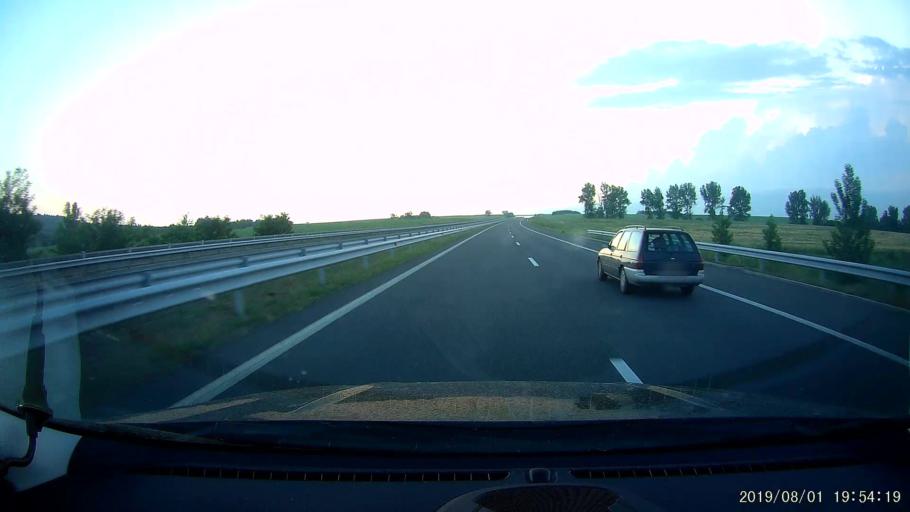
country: BG
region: Burgas
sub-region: Obshtina Karnobat
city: Karnobat
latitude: 42.5768
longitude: 26.9036
